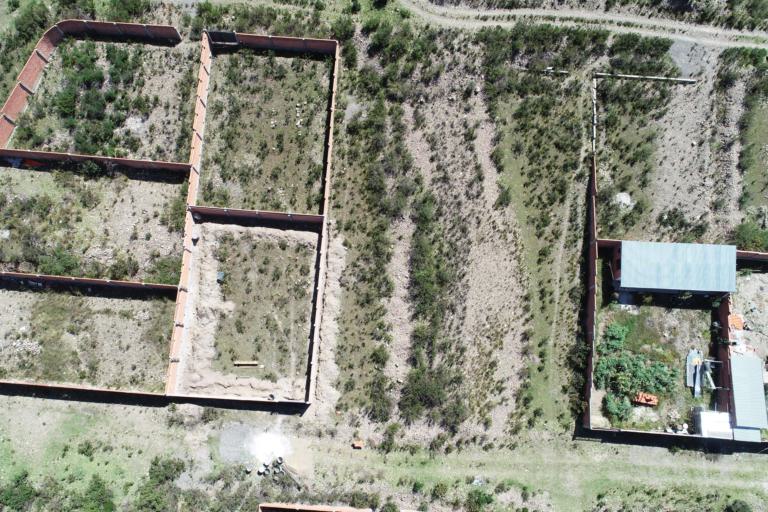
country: BO
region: La Paz
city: La Paz
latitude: -16.5030
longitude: -68.0584
